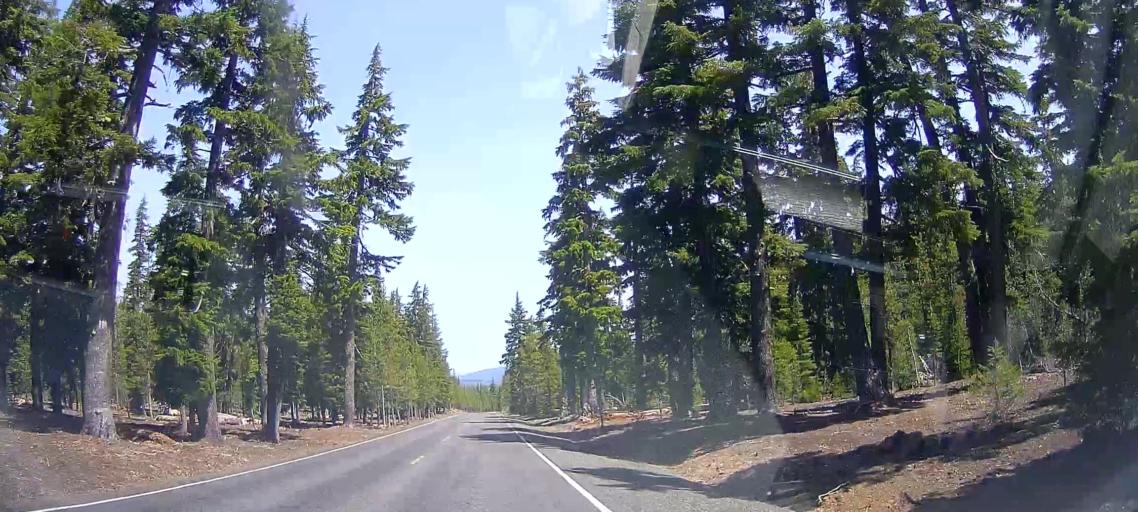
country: US
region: Oregon
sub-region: Jackson County
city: Shady Cove
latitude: 43.0009
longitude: -122.1346
